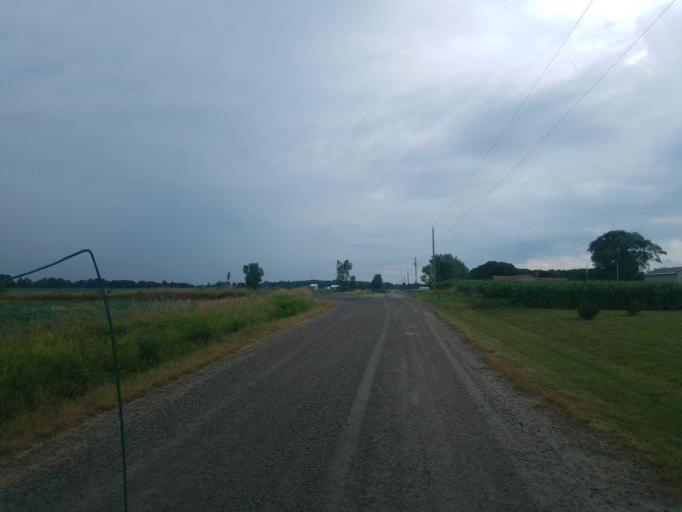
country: US
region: Ohio
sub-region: Defiance County
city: Hicksville
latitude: 41.3505
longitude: -84.8040
